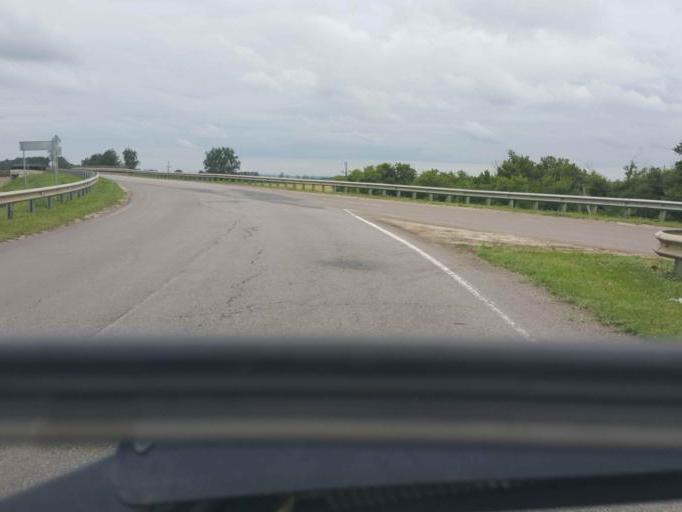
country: RU
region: Tambov
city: Zavoronezhskoye
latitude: 52.9103
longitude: 40.6357
